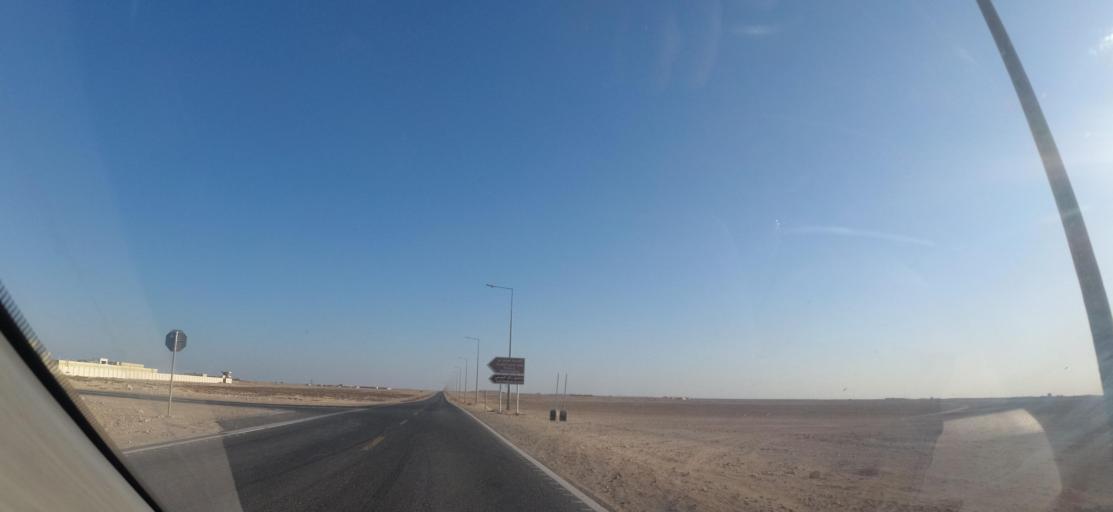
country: QA
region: Madinat ash Shamal
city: Ar Ru'ays
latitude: 26.1295
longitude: 51.2336
